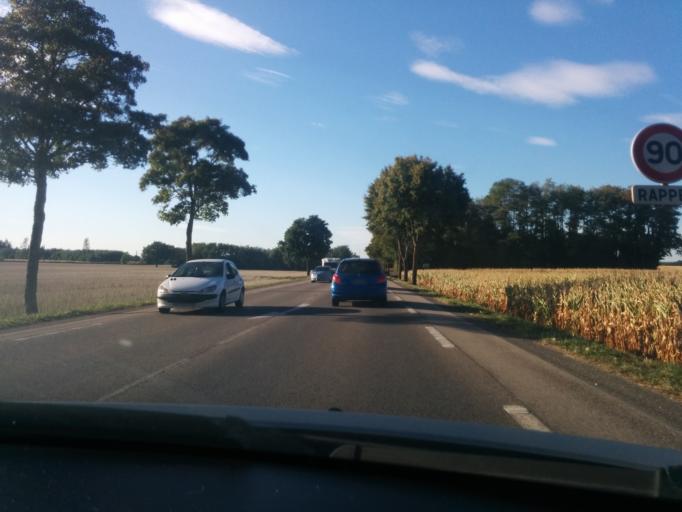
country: FR
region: Rhone-Alpes
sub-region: Departement de l'Ain
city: Tossiat
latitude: 46.1262
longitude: 5.2932
